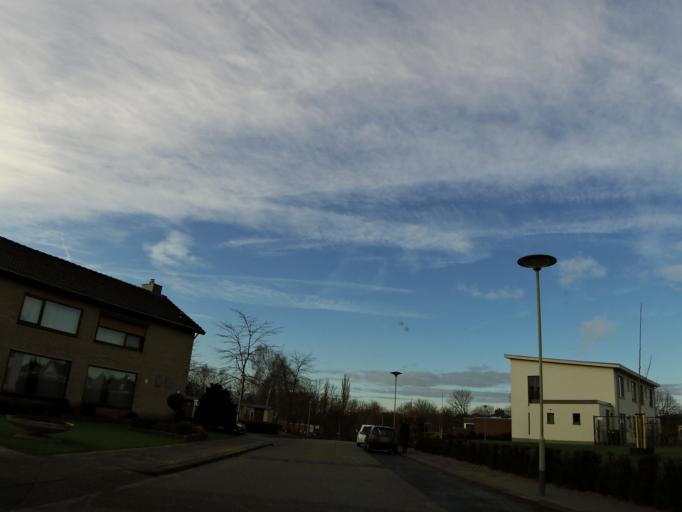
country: NL
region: Limburg
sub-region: Gemeente Heerlen
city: Heerlen
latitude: 50.8922
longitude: 6.0077
